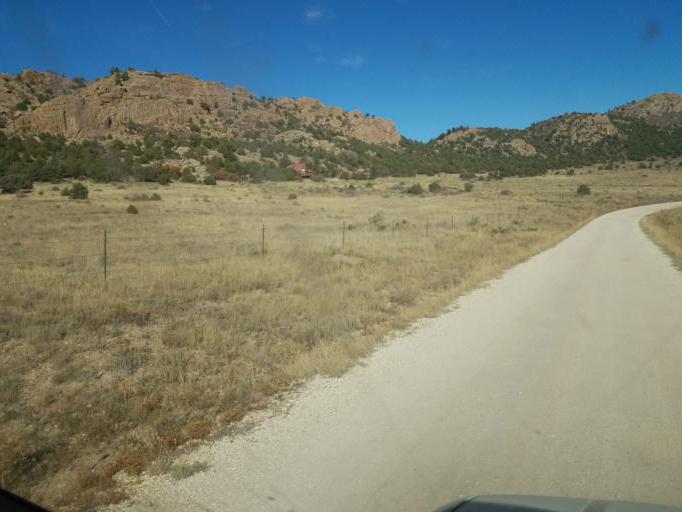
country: US
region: Colorado
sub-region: Custer County
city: Westcliffe
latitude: 38.2346
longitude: -105.4617
